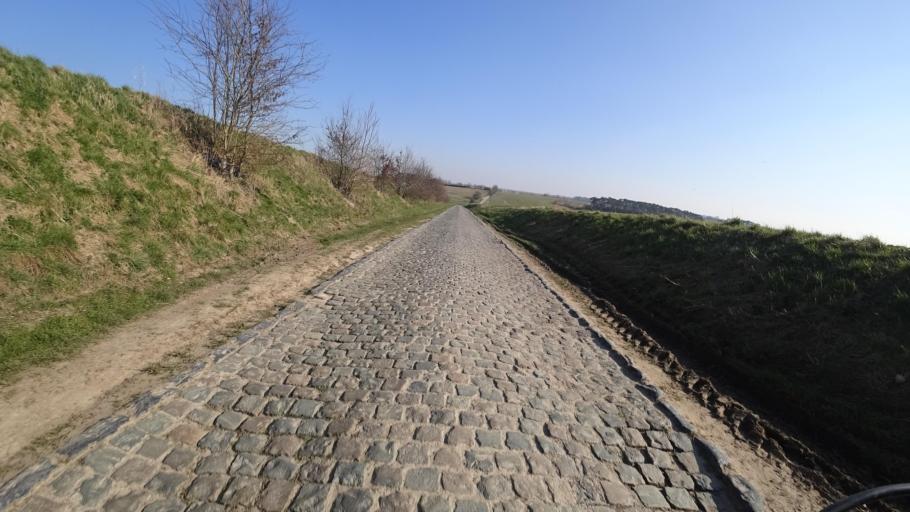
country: BE
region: Wallonia
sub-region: Province du Brabant Wallon
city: Mont-Saint-Guibert
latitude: 50.6078
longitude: 4.5917
